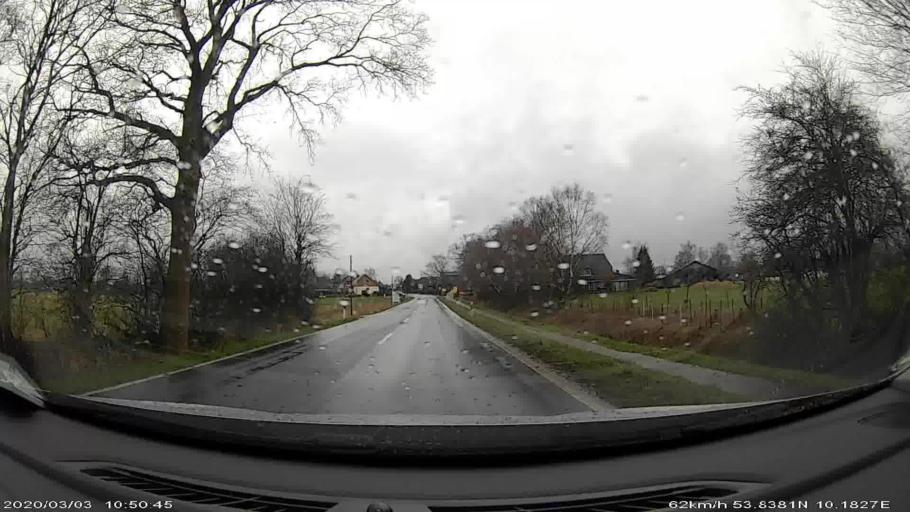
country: DE
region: Schleswig-Holstein
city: Seth
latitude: 53.8403
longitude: 10.1807
